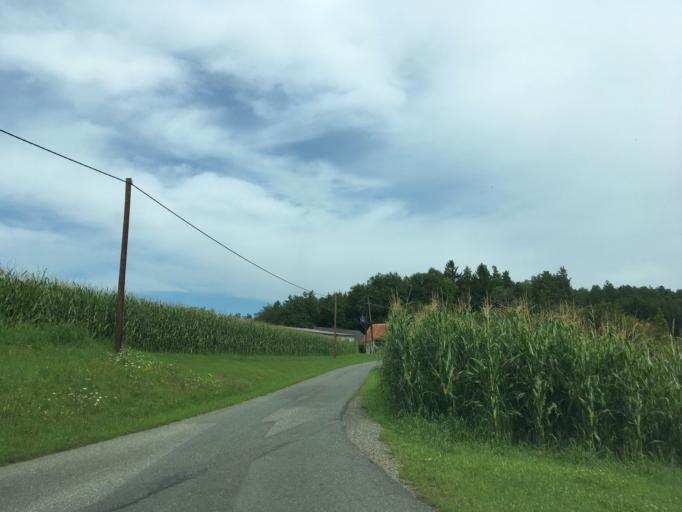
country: AT
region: Styria
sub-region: Politischer Bezirk Deutschlandsberg
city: Wettmannstatten
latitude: 46.7963
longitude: 15.3992
